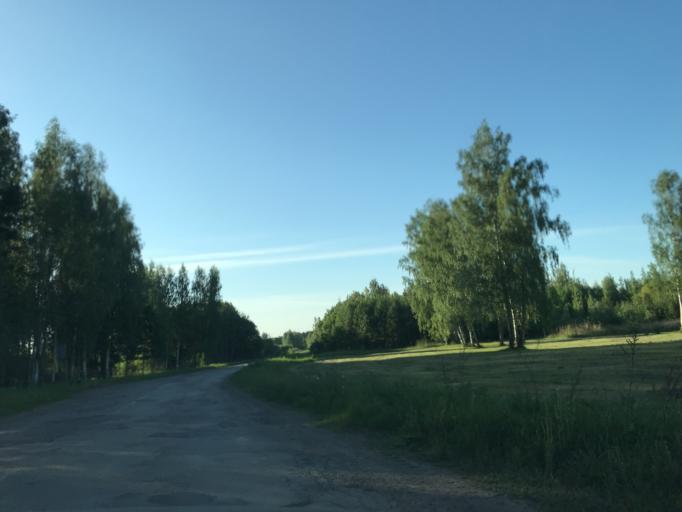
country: LV
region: Ozolnieku
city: Ozolnieki
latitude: 56.5928
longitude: 23.8056
